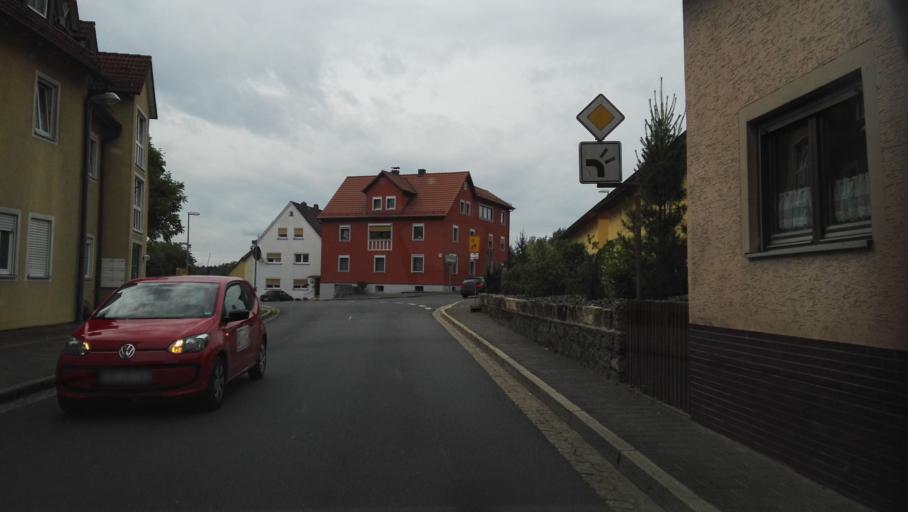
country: DE
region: Bavaria
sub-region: Upper Franconia
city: Hollfeld
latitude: 49.9382
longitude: 11.2890
